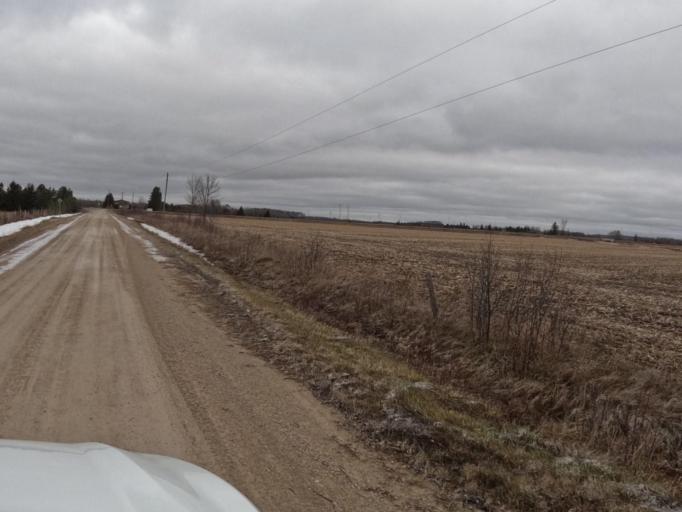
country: CA
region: Ontario
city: Shelburne
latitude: 44.0371
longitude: -80.3727
